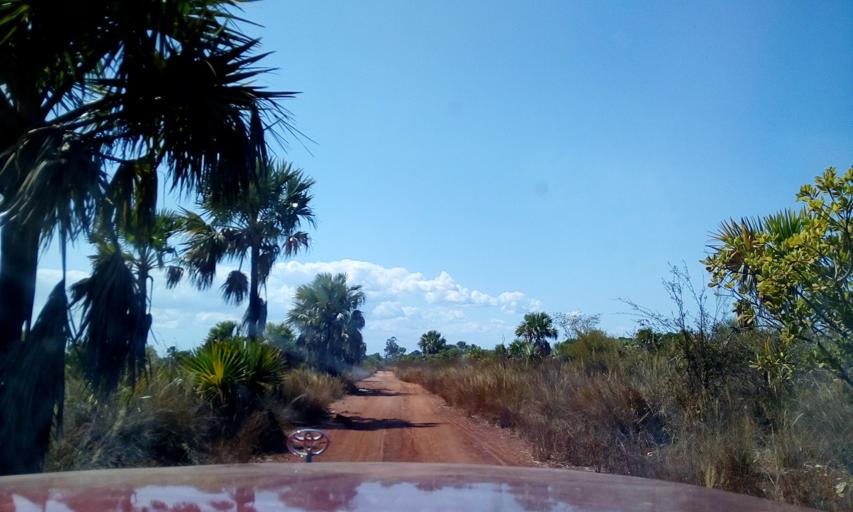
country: MG
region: Boeny
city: Sitampiky
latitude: -16.1190
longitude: 45.4637
